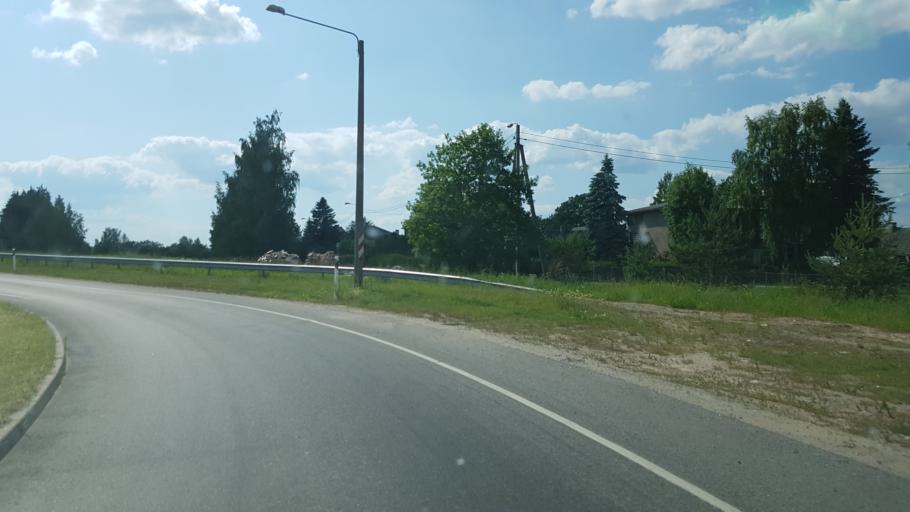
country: EE
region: Jogevamaa
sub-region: Jogeva linn
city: Jogeva
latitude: 58.7555
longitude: 26.4010
